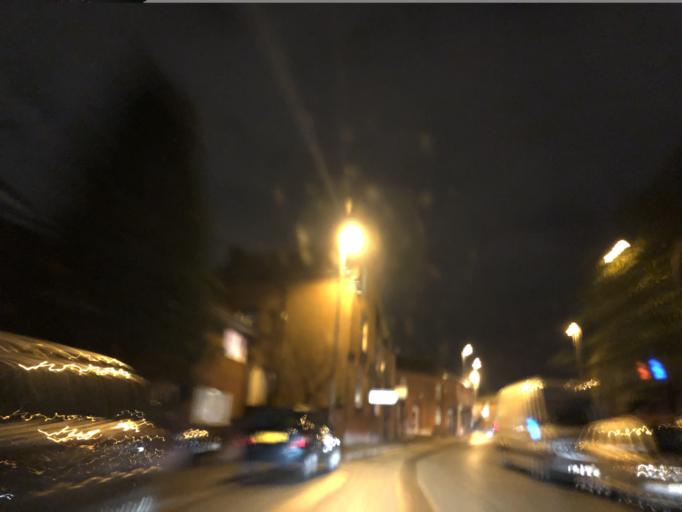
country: GB
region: England
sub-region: Borough of Oldham
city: Oldham
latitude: 53.5260
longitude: -2.1121
